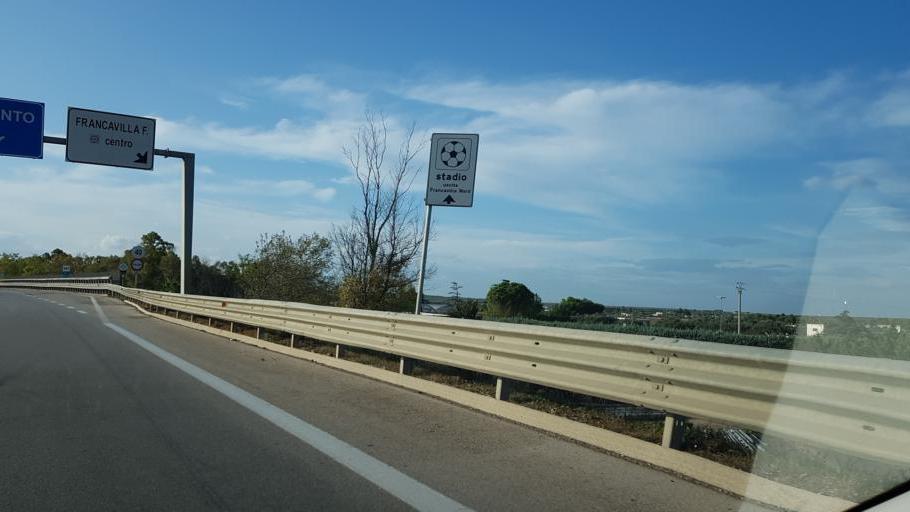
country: IT
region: Apulia
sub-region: Provincia di Brindisi
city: Francavilla Fontana
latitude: 40.5459
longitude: 17.5947
